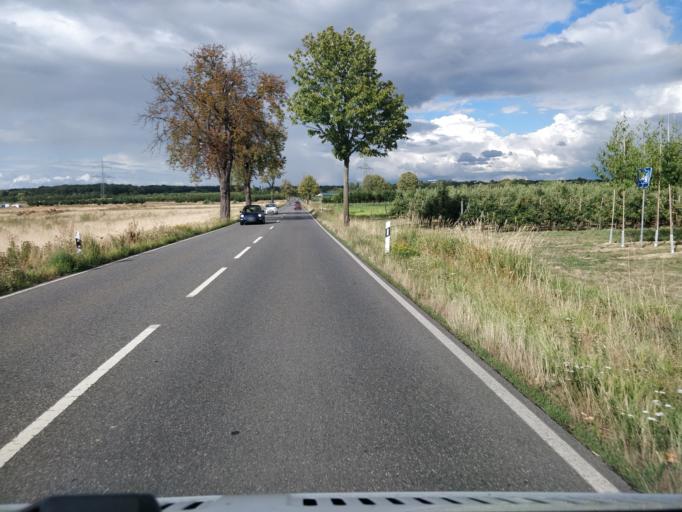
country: DE
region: North Rhine-Westphalia
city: Meckenheim
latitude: 50.6329
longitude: 7.0281
